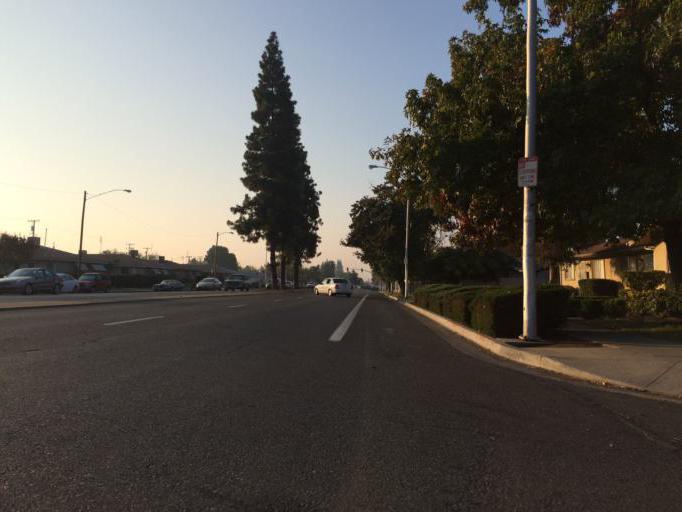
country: US
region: California
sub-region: Fresno County
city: Fresno
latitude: 36.7741
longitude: -119.7727
